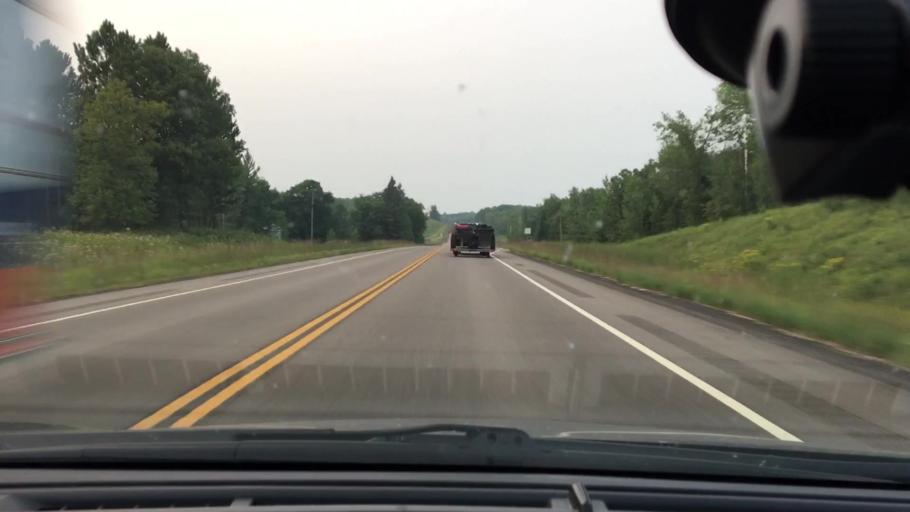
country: US
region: Minnesota
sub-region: Crow Wing County
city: Crosby
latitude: 46.6113
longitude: -93.9489
